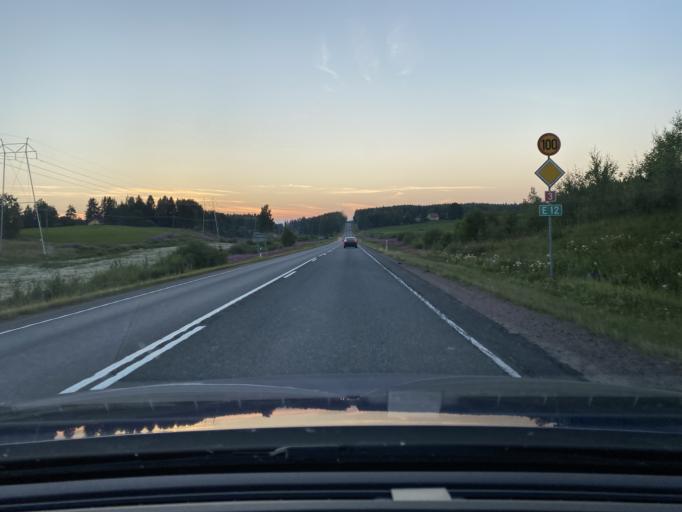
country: FI
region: Pirkanmaa
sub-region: Luoteis-Pirkanmaa
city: Ikaalinen
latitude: 61.8109
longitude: 22.9602
